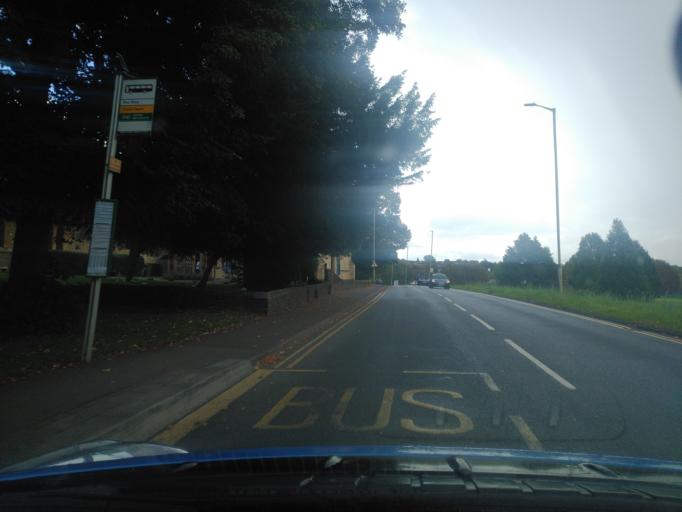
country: GB
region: England
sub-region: Hertfordshire
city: Hemel Hempstead
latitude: 51.7442
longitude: -0.4793
